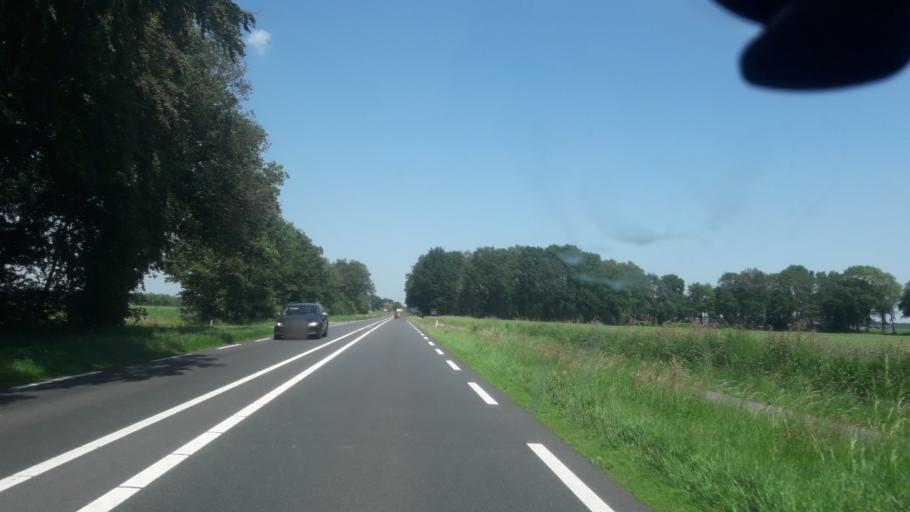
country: NL
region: Overijssel
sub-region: Gemeente Deventer
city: Schalkhaar
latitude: 52.3124
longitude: 6.2061
